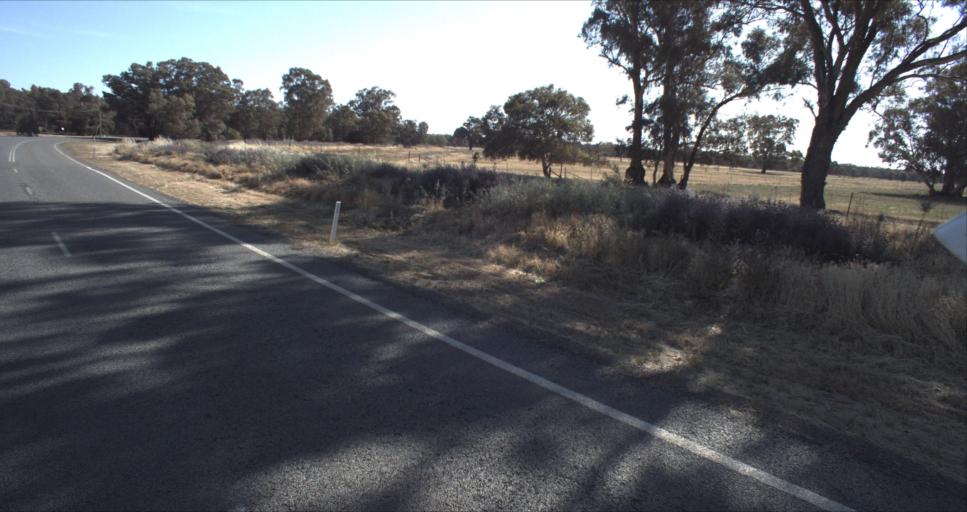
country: AU
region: New South Wales
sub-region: Leeton
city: Leeton
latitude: -34.6240
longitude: 146.3951
